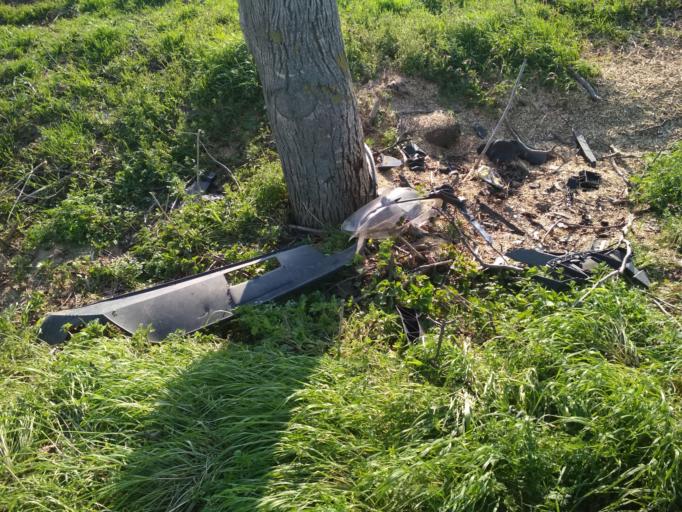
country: HU
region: Tolna
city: Bonyhad
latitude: 46.3333
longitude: 18.5173
